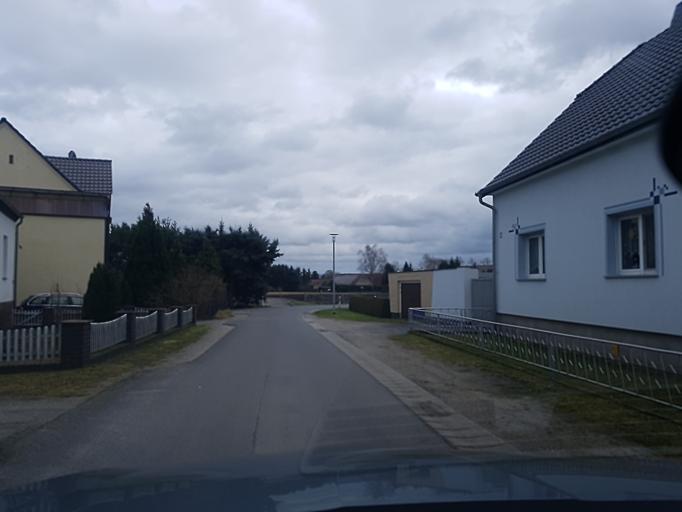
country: DE
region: Brandenburg
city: Schonborn
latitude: 51.5986
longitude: 13.4966
